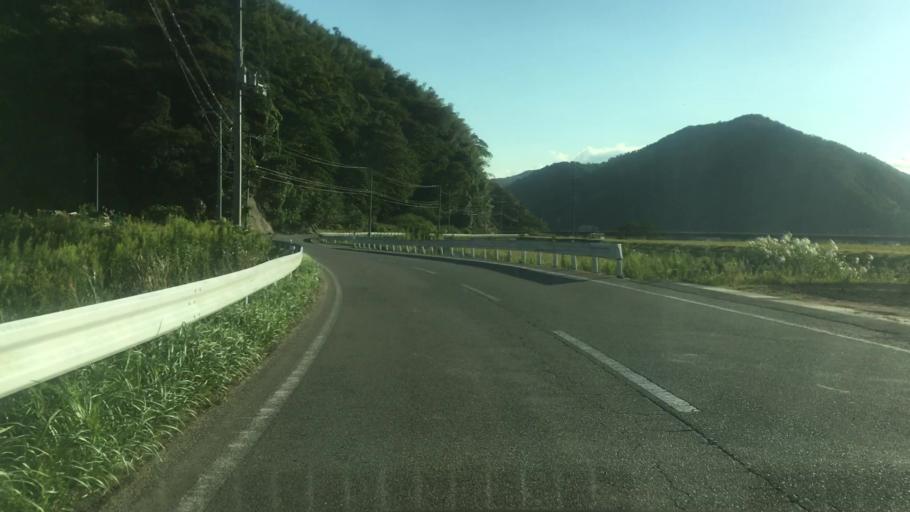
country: JP
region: Hyogo
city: Toyooka
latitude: 35.6104
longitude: 134.8089
